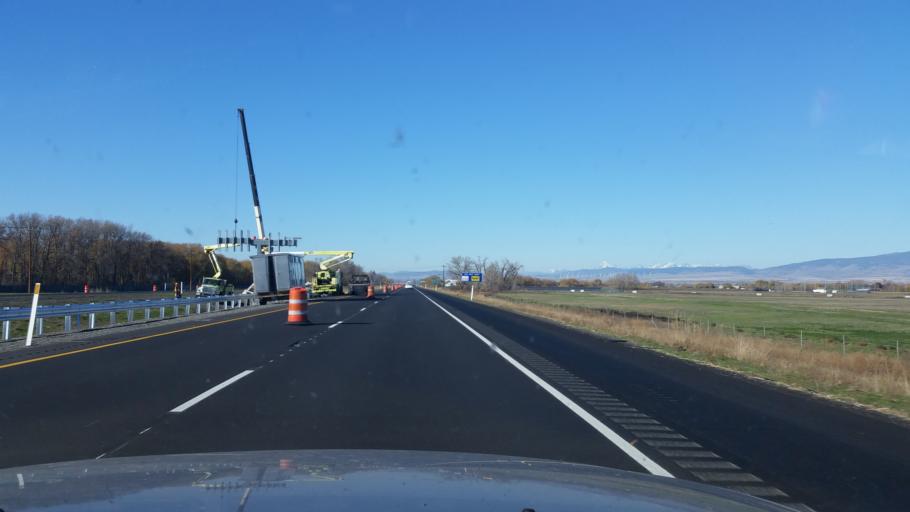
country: US
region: Washington
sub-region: Kittitas County
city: Ellensburg
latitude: 46.9855
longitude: -120.5656
